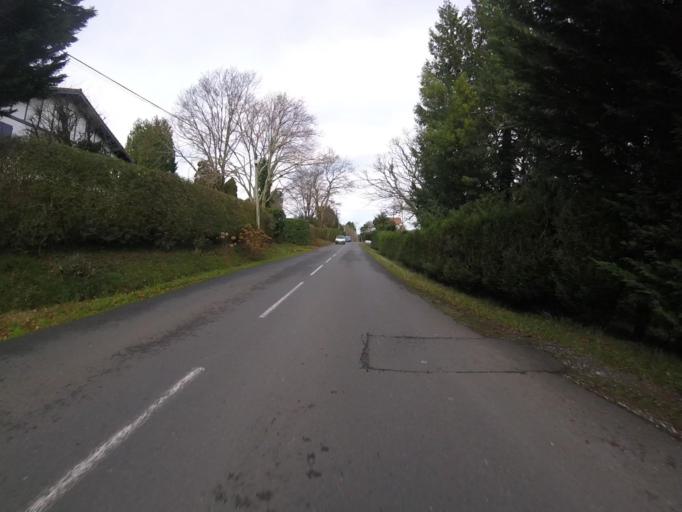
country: FR
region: Aquitaine
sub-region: Departement des Pyrenees-Atlantiques
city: Saint-Jean-de-Luz
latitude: 43.3680
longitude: -1.6569
